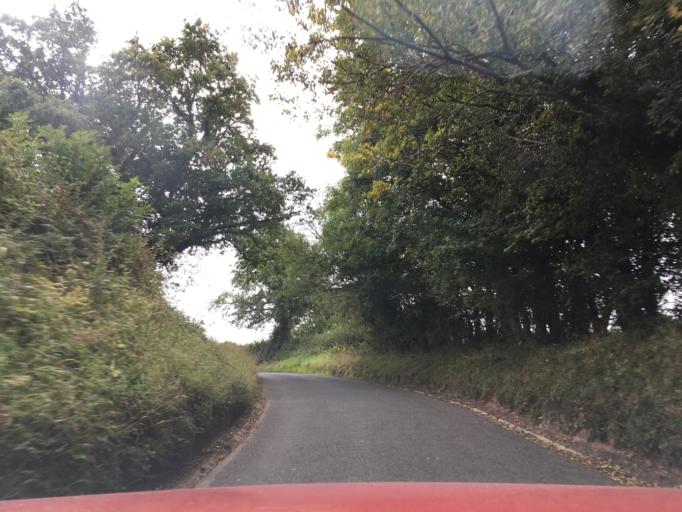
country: GB
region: England
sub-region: South Gloucestershire
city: Charfield
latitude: 51.6456
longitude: -2.4270
